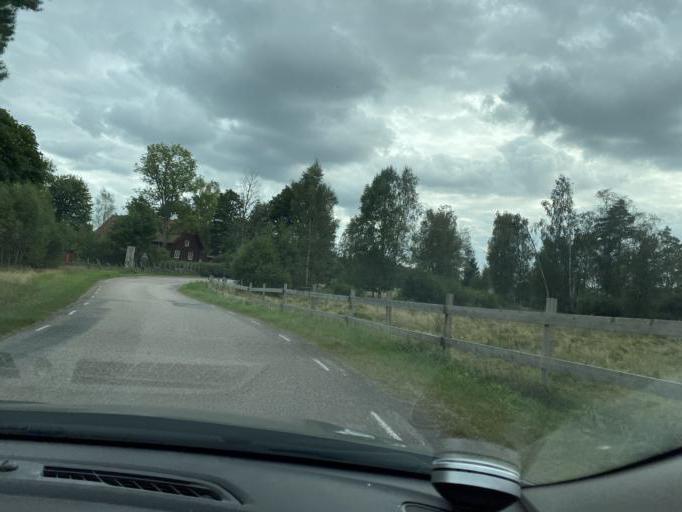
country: SE
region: Kronoberg
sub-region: Markaryds Kommun
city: Markaryd
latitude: 56.4763
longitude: 13.5649
